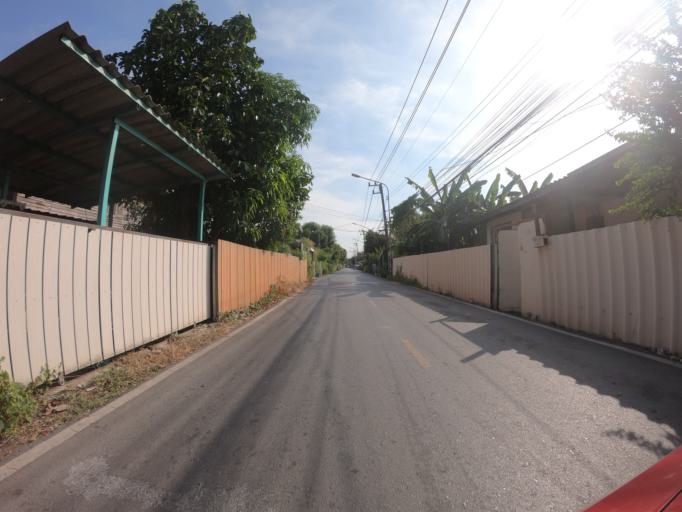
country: TH
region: Pathum Thani
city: Thanyaburi
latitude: 14.0150
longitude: 100.7325
